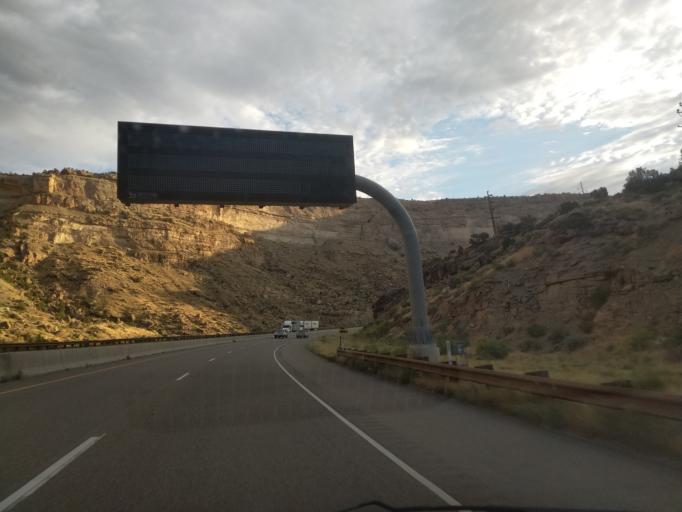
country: US
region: Colorado
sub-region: Mesa County
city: Palisade
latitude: 39.1921
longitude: -108.2816
